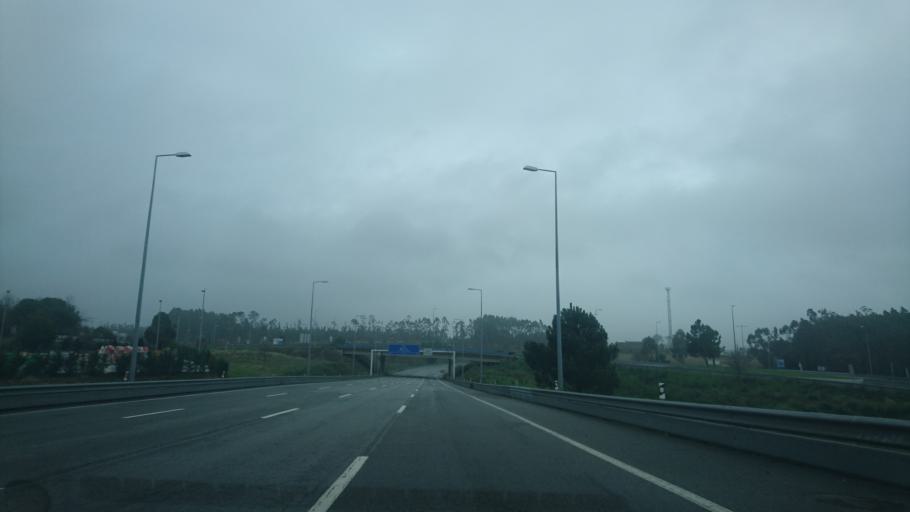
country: PT
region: Porto
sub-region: Matosinhos
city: Santa Cruz do Bispo
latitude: 41.2238
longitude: -8.6672
